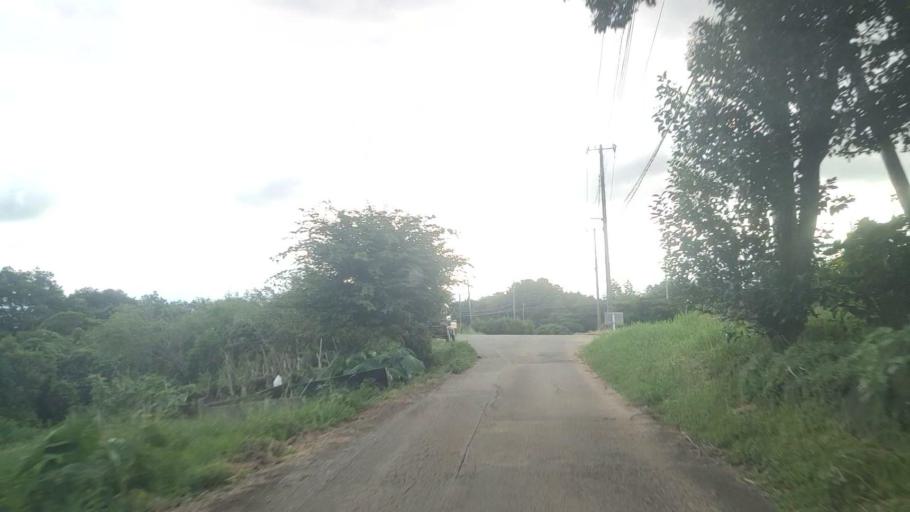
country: JP
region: Shizuoka
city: Mishima
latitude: 35.1248
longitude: 138.9880
